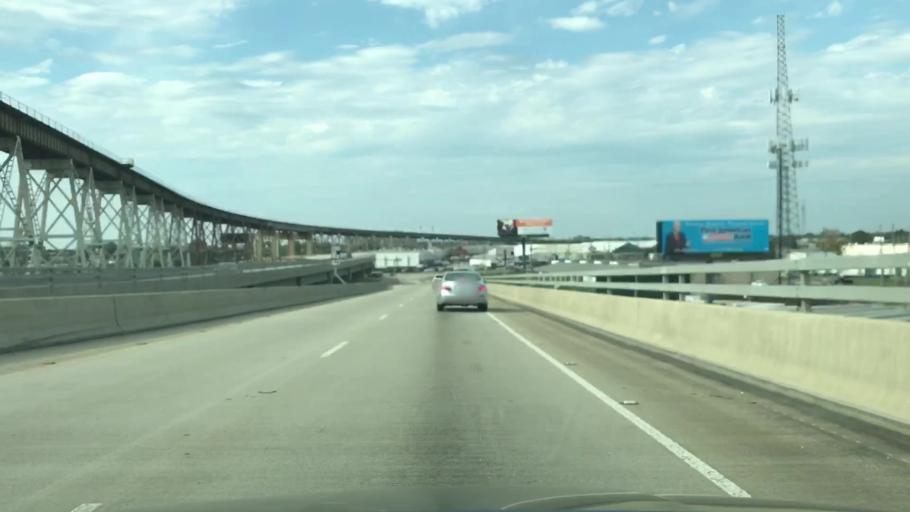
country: US
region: Louisiana
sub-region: Jefferson Parish
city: Elmwood
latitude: 29.9512
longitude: -90.1764
